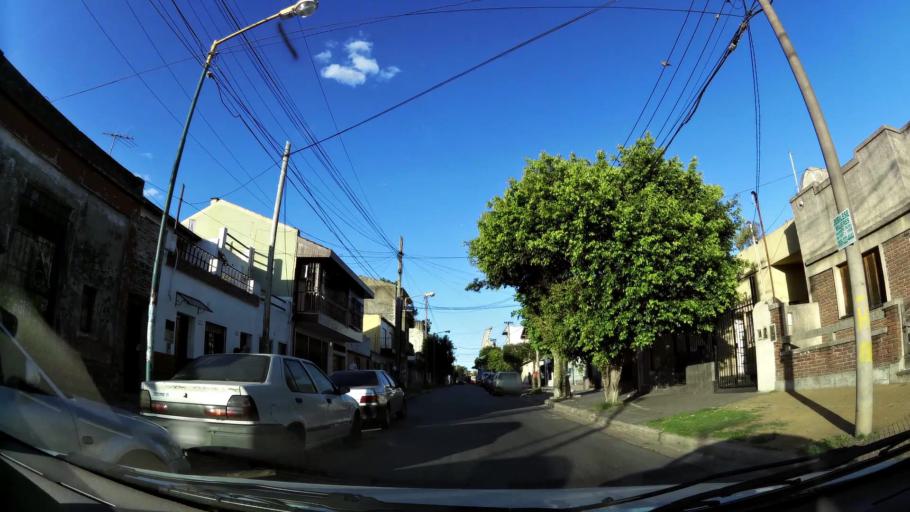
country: AR
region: Buenos Aires
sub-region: Partido de General San Martin
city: General San Martin
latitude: -34.5683
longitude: -58.5302
